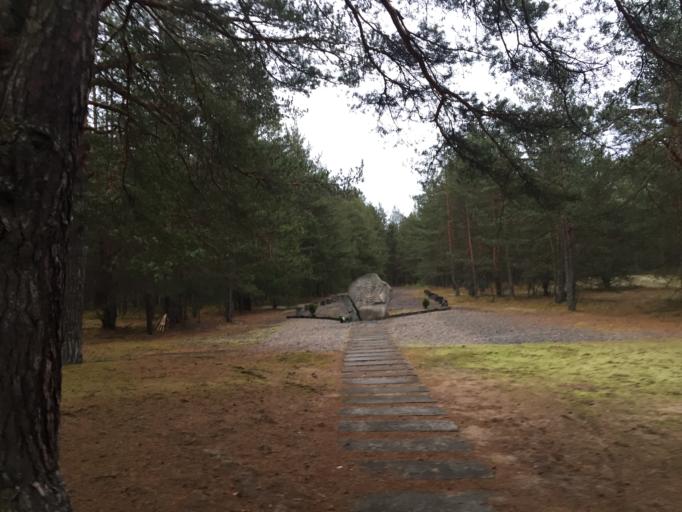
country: LV
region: Daugavpils
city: Daugavpils
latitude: 55.9064
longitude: 26.4670
